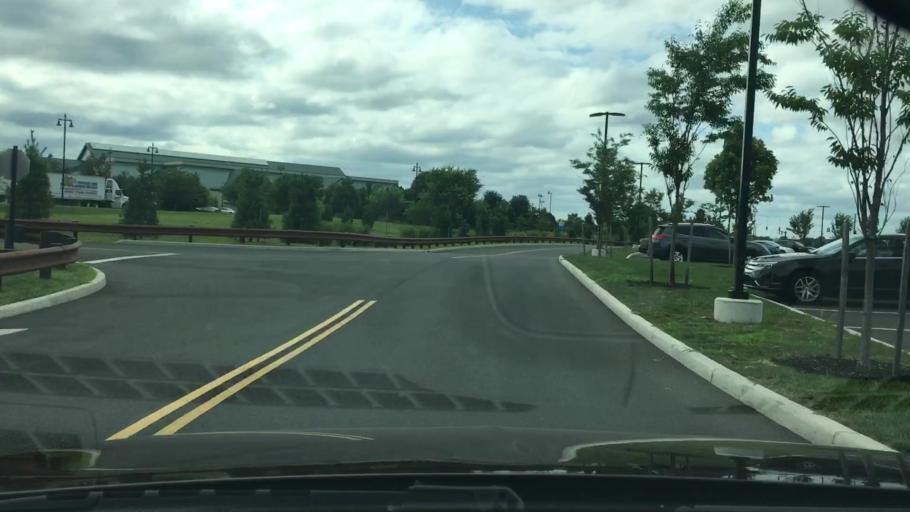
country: US
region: Connecticut
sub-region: Hartford County
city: East Hartford
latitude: 41.7582
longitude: -72.6234
